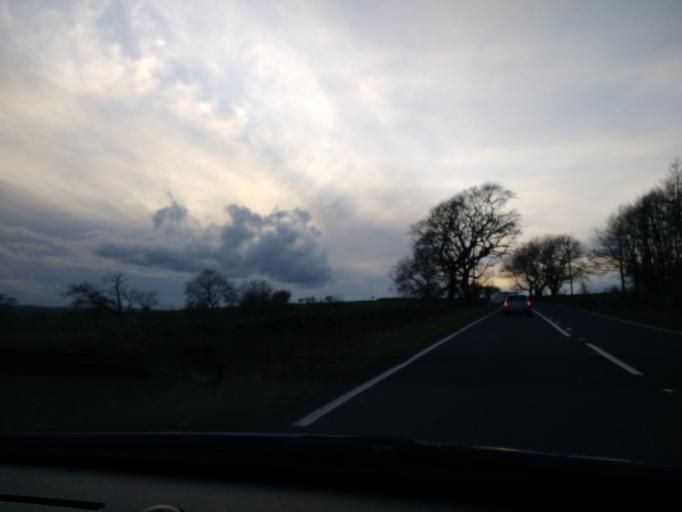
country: GB
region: England
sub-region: North Yorkshire
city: Ingleton
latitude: 54.1230
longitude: -2.4078
